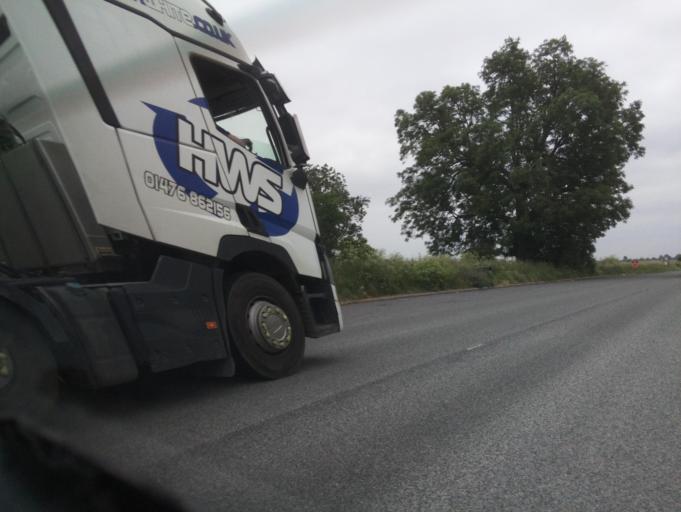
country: GB
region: England
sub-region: District of Rutland
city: Exton
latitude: 52.6731
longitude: -0.6538
